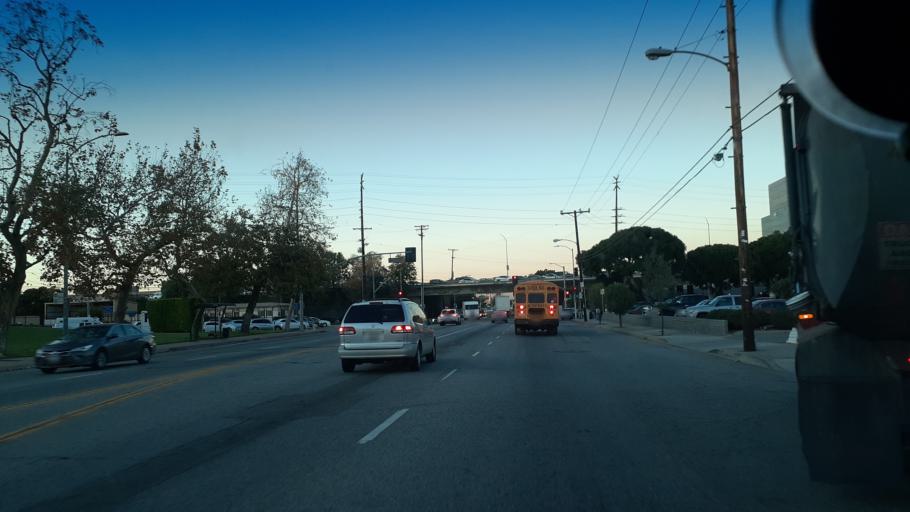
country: US
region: California
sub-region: Los Angeles County
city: Carson
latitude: 33.8579
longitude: -118.2905
